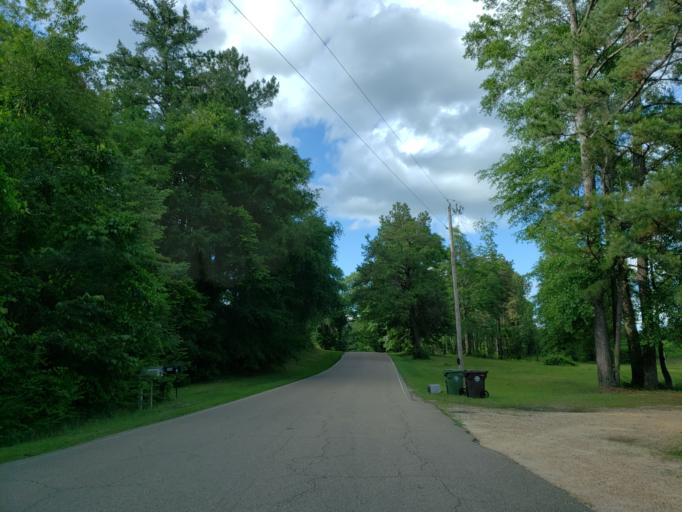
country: US
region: Mississippi
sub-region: Forrest County
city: Hattiesburg
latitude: 31.2479
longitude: -89.2417
